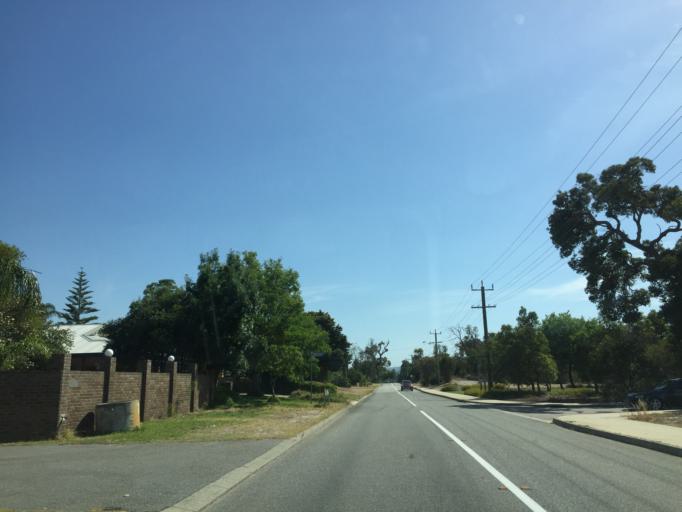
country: AU
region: Western Australia
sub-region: Gosnells
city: Southern River
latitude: -32.0837
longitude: 115.9585
